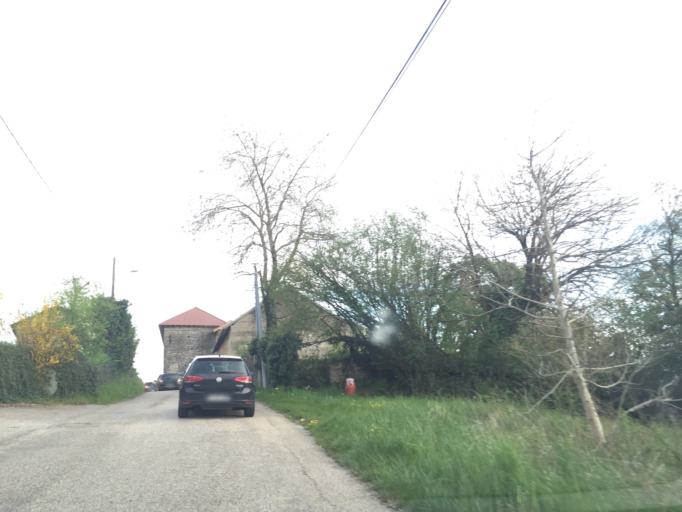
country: FR
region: Rhone-Alpes
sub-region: Departement de l'Isere
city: Salagnon
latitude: 45.7301
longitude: 5.3774
